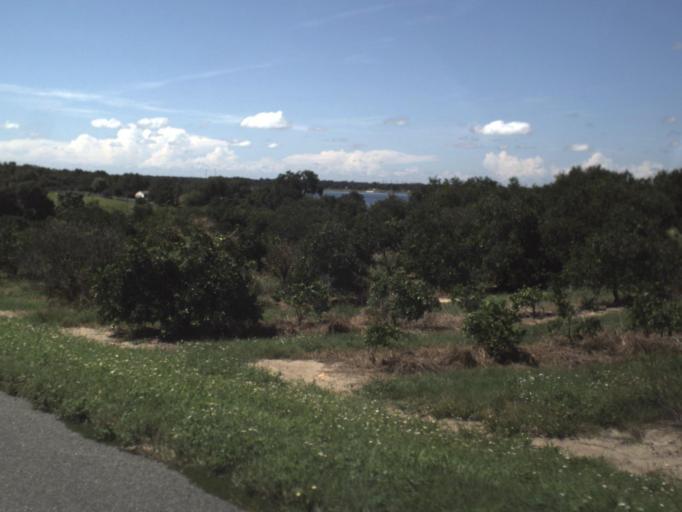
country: US
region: Florida
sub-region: Polk County
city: Dundee
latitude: 28.0024
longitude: -81.5950
